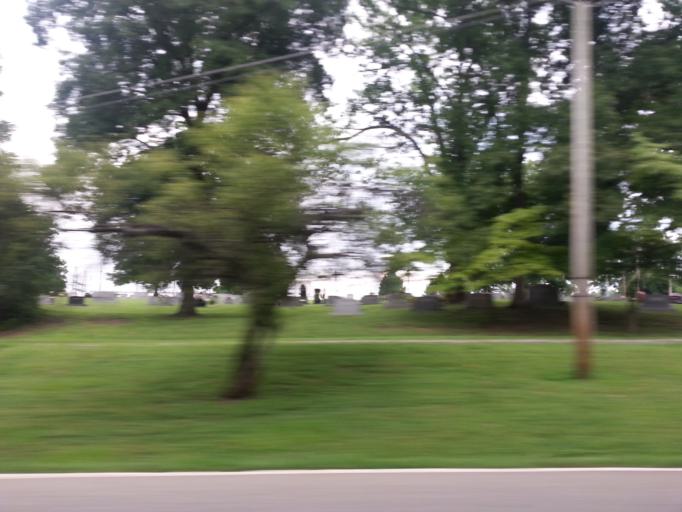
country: US
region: Tennessee
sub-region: Loudon County
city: Greenback
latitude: 35.6530
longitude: -84.1540
